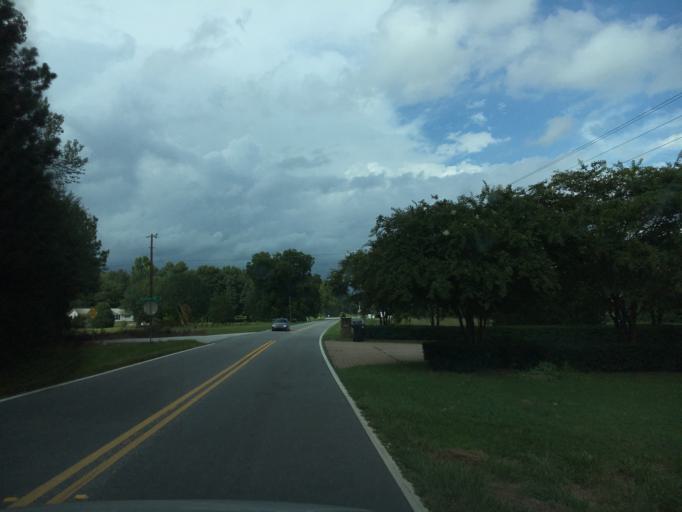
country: US
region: Georgia
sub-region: Rockdale County
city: Lakeview Estates
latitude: 33.7657
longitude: -84.0010
